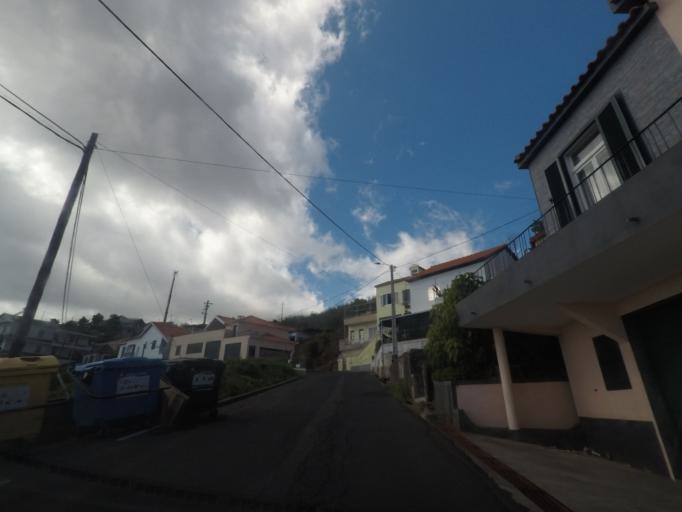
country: PT
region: Madeira
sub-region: Ribeira Brava
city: Campanario
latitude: 32.6732
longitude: -17.0499
